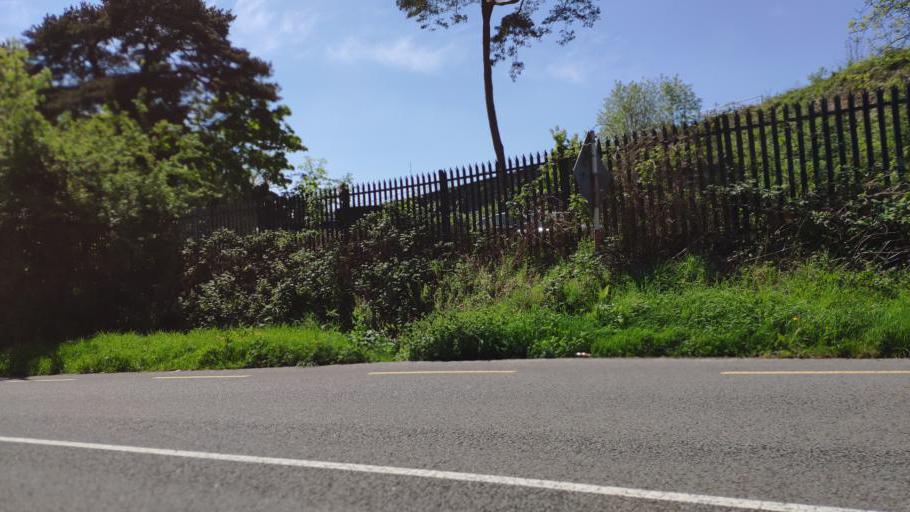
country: IE
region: Munster
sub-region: County Cork
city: Cork
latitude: 51.9278
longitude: -8.4875
